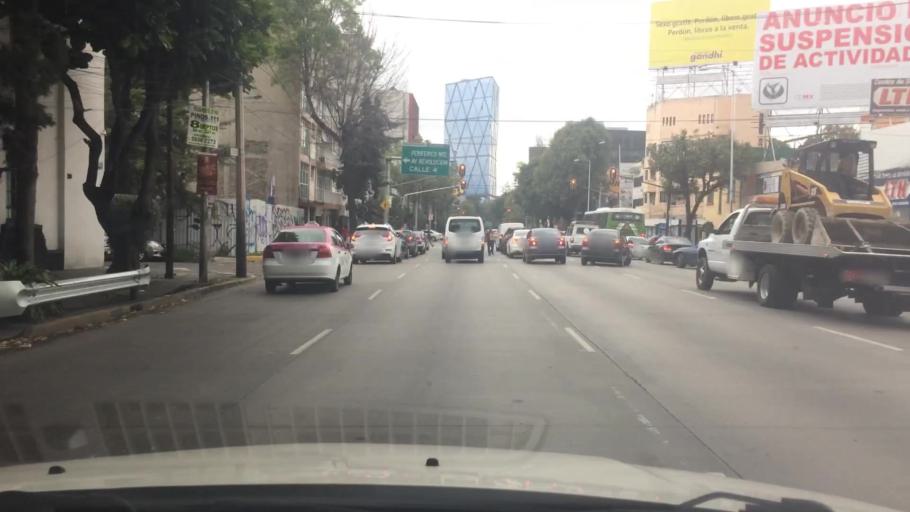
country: MX
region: Mexico City
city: Colonia del Valle
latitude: 19.3905
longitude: -99.1823
